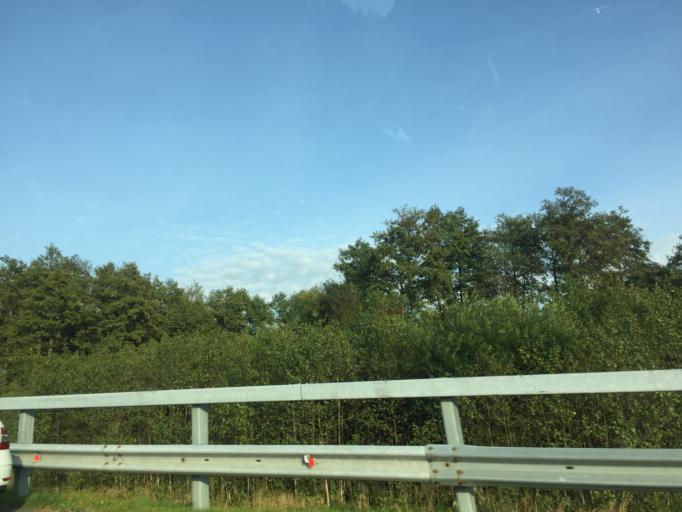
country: RU
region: Kaliningrad
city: Gur'yevsk
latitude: 54.8788
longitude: 20.5869
